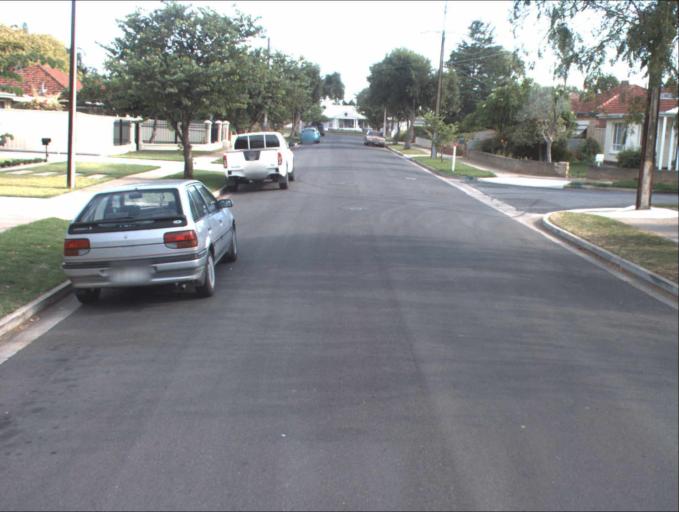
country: AU
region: South Australia
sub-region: Port Adelaide Enfield
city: Klemzig
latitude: -34.8741
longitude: 138.6204
